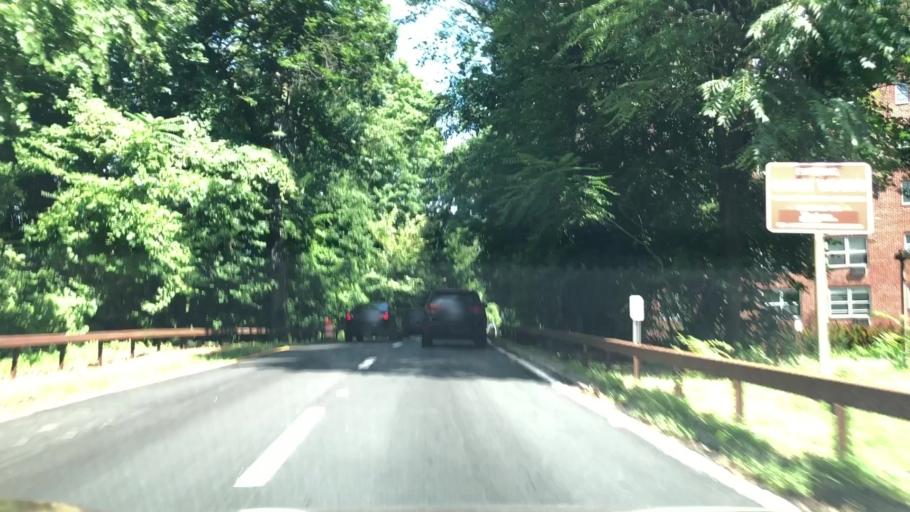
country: US
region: New York
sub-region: Westchester County
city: Greenville
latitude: 40.9807
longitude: -73.8137
